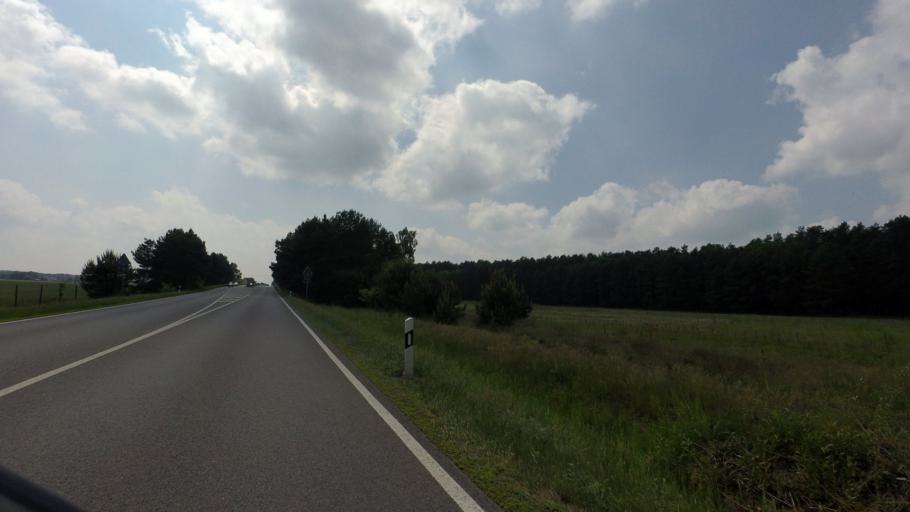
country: DE
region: Brandenburg
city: Cottbus
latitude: 51.6923
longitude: 14.3603
